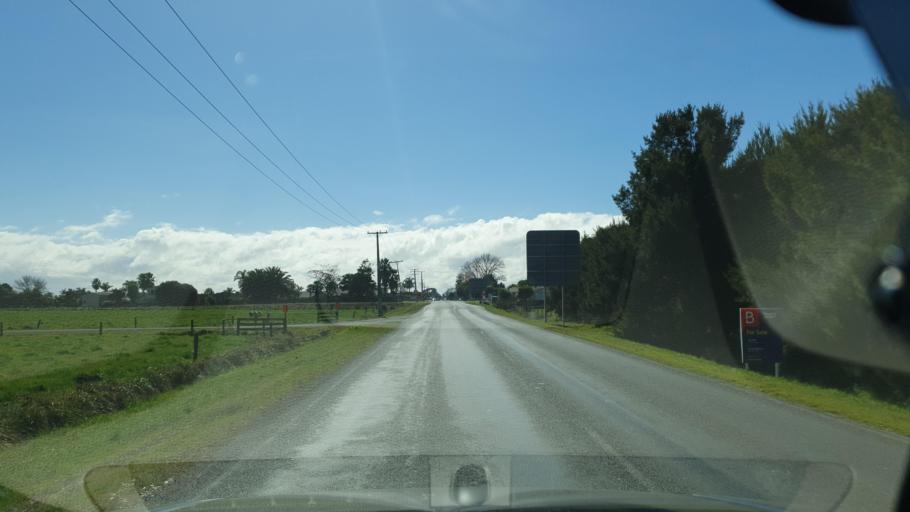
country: NZ
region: Bay of Plenty
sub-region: Tauranga City
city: Tauranga
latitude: -37.7106
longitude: 176.2847
